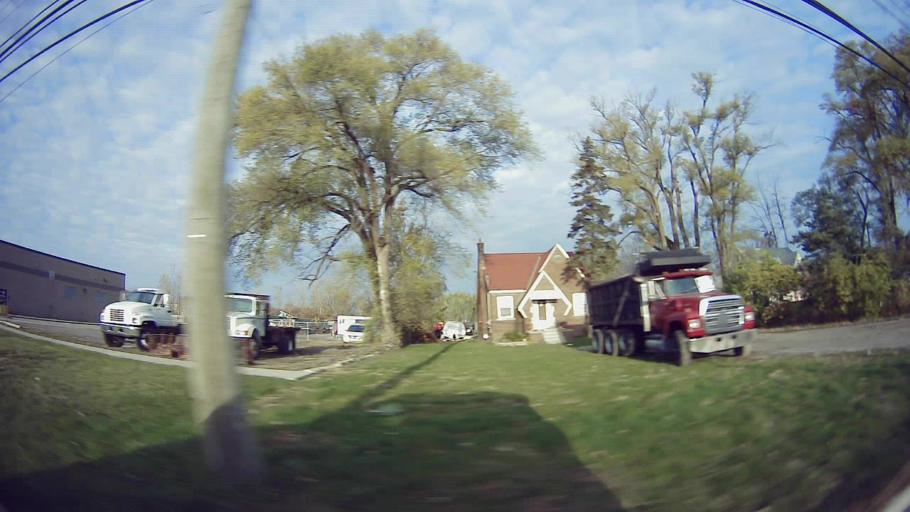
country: US
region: Michigan
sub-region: Macomb County
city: Mount Clemens
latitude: 42.5492
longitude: -82.8749
